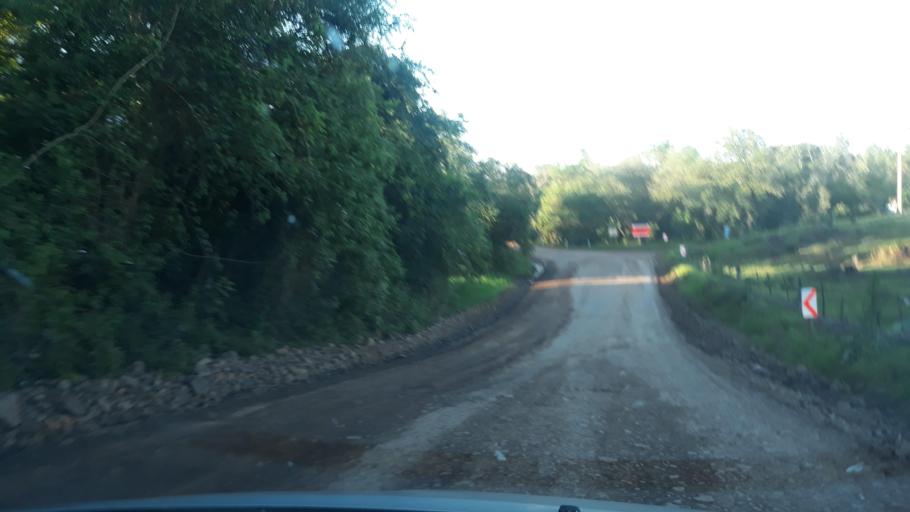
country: AR
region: Misiones
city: Ruiz de Montoya
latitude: -27.0465
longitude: -55.0036
